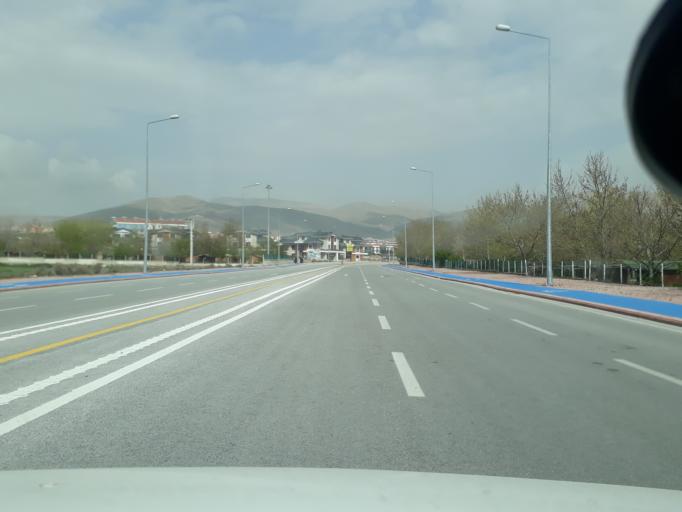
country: TR
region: Konya
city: Sille
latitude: 37.9480
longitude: 32.4773
